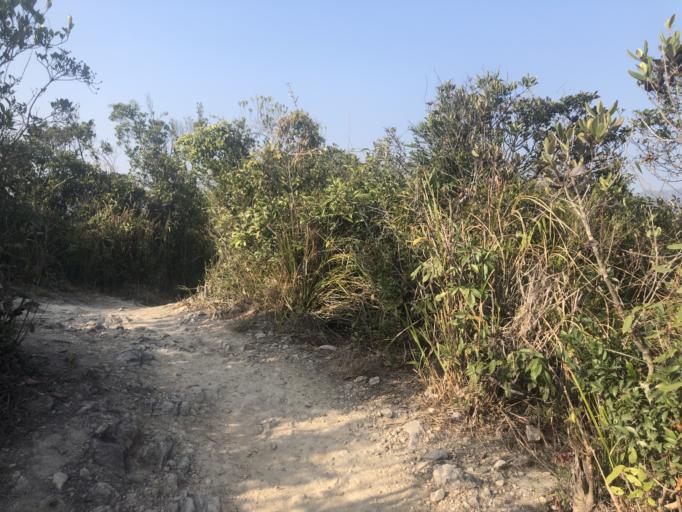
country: HK
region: Sai Kung
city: Sai Kung
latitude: 22.3600
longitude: 114.2947
